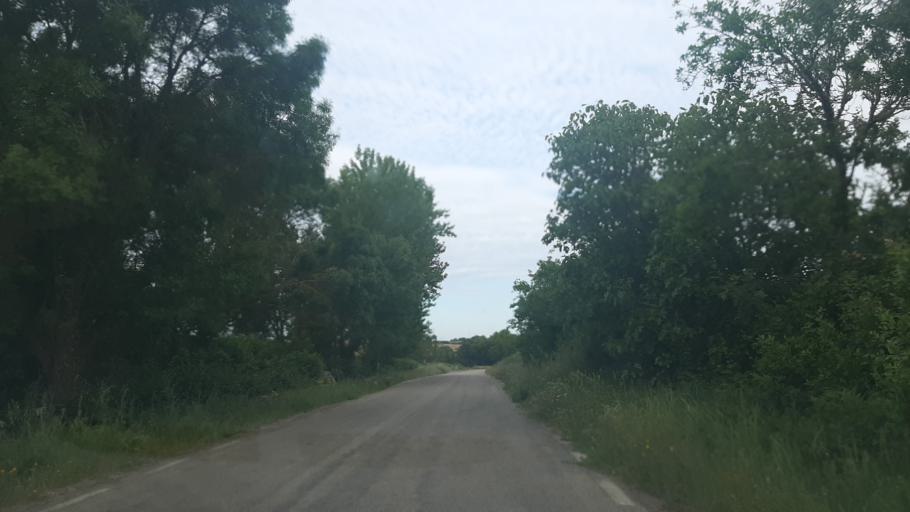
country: ES
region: Castille and Leon
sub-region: Provincia de Salamanca
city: Gallegos de Arganan
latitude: 40.6467
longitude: -6.7498
